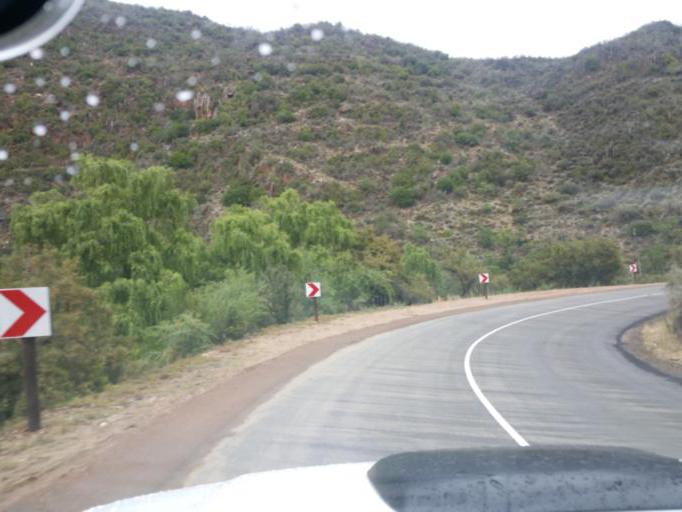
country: ZA
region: Western Cape
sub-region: Eden District Municipality
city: Oudtshoorn
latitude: -33.4220
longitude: 22.2422
